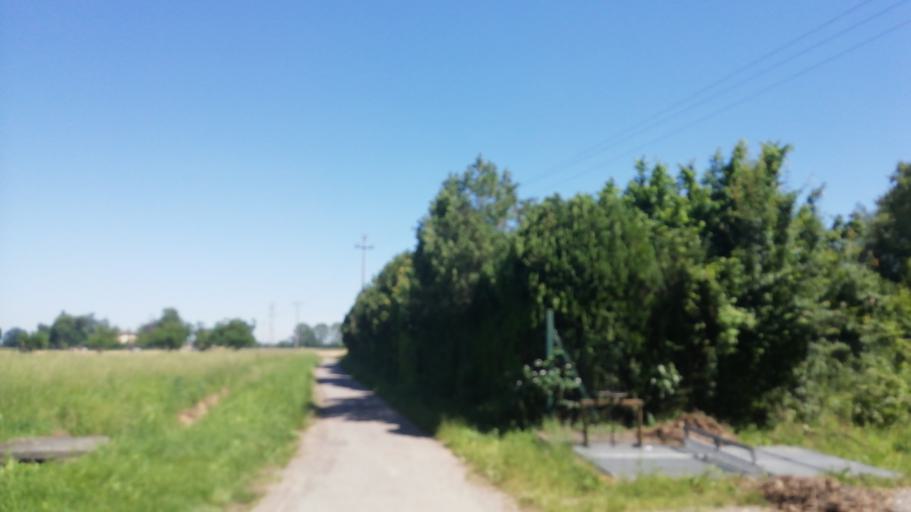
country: IT
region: Emilia-Romagna
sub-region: Provincia di Piacenza
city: Borgonovo Valtidone
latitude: 45.0023
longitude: 9.4511
